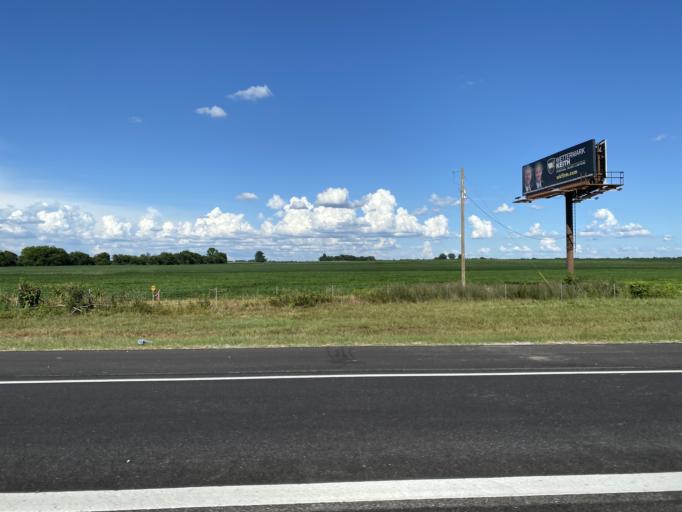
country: US
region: Alabama
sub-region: Limestone County
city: Athens
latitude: 34.7354
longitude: -86.9376
